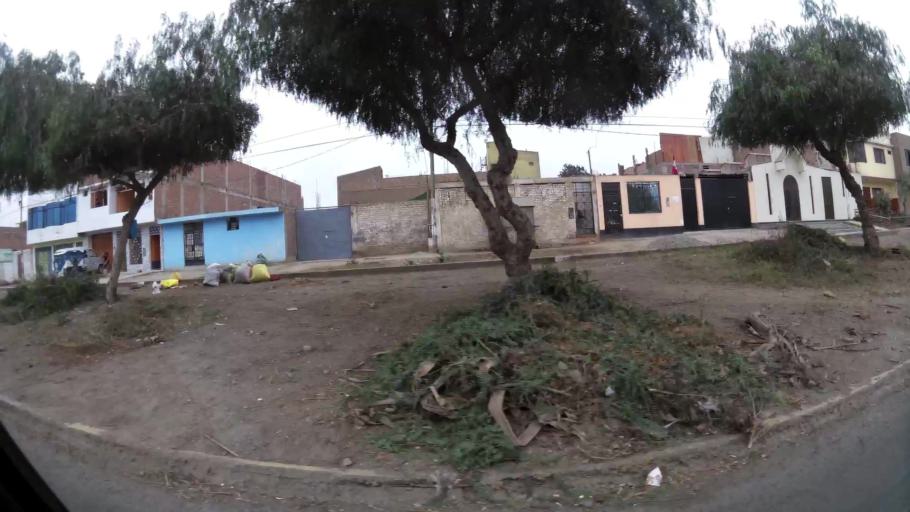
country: PE
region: Lima
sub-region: Lima
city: Urb. Santo Domingo
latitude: -11.8766
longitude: -77.0662
